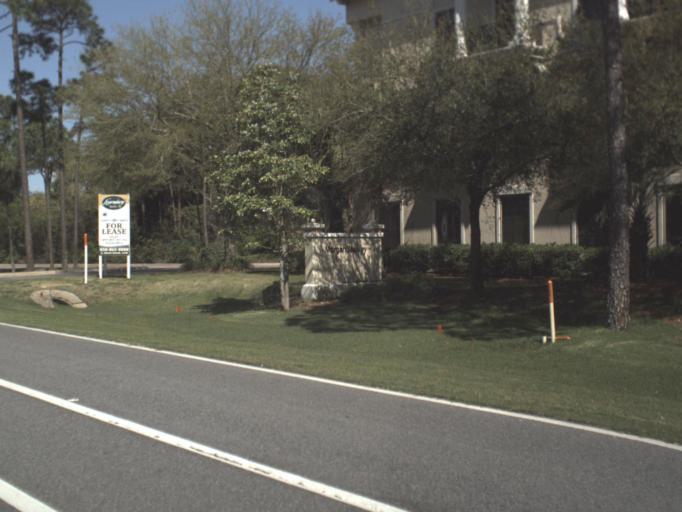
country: US
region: Florida
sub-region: Walton County
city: Miramar Beach
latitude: 30.3890
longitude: -86.4154
